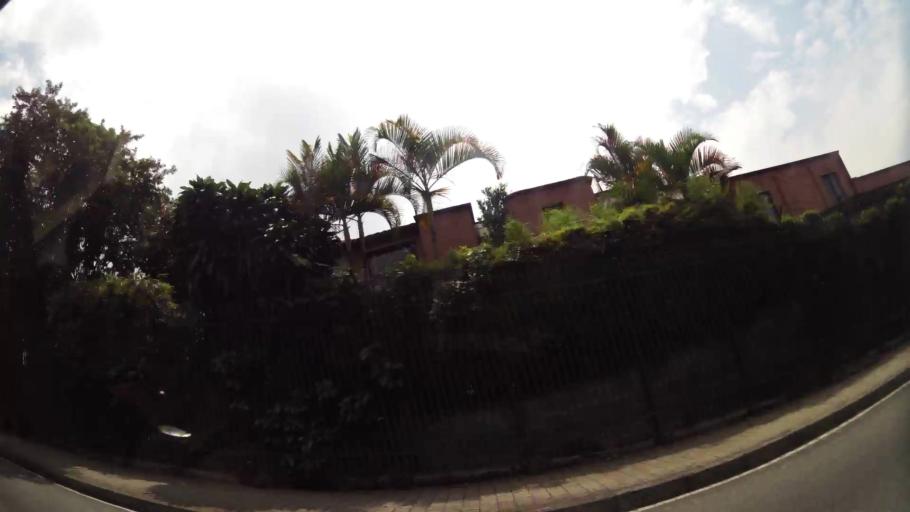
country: CO
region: Antioquia
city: Envigado
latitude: 6.1919
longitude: -75.5692
